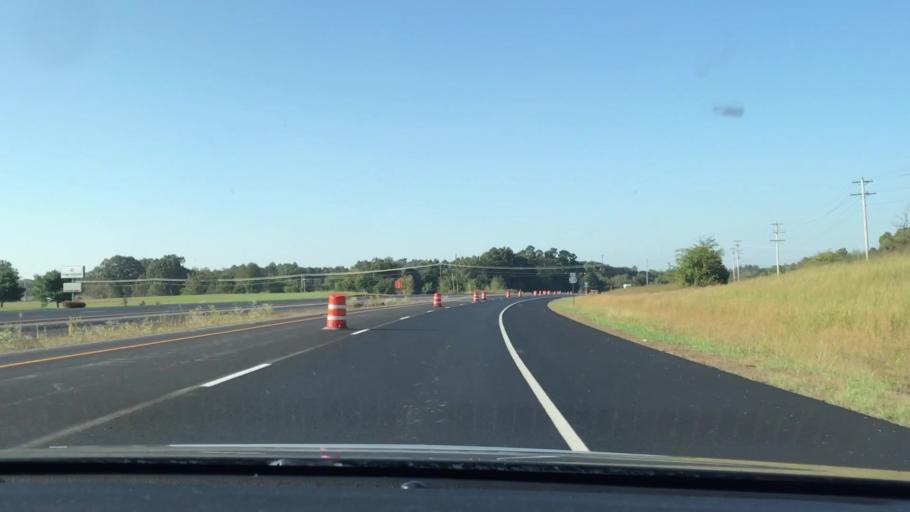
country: US
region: Kentucky
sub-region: Trigg County
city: Cadiz
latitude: 36.8455
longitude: -87.8233
